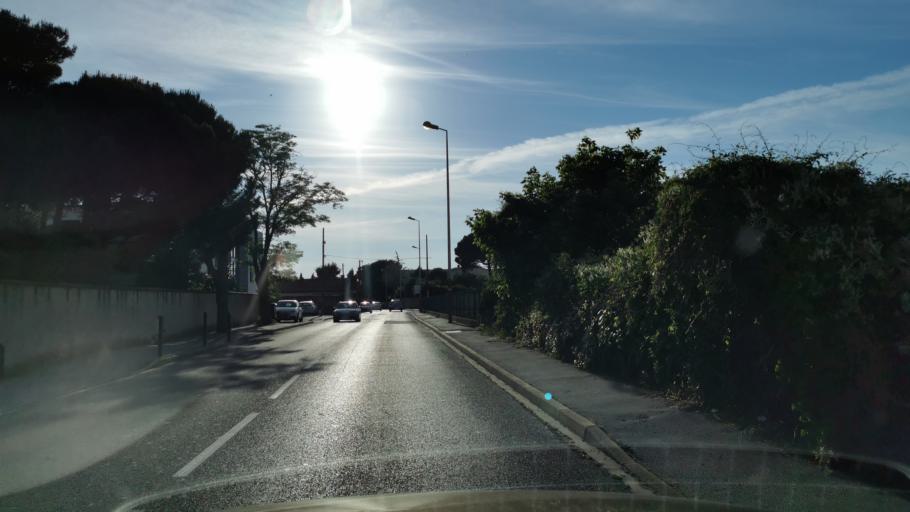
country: FR
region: Languedoc-Roussillon
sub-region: Departement de l'Aude
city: Narbonne
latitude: 43.1834
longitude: 3.0295
